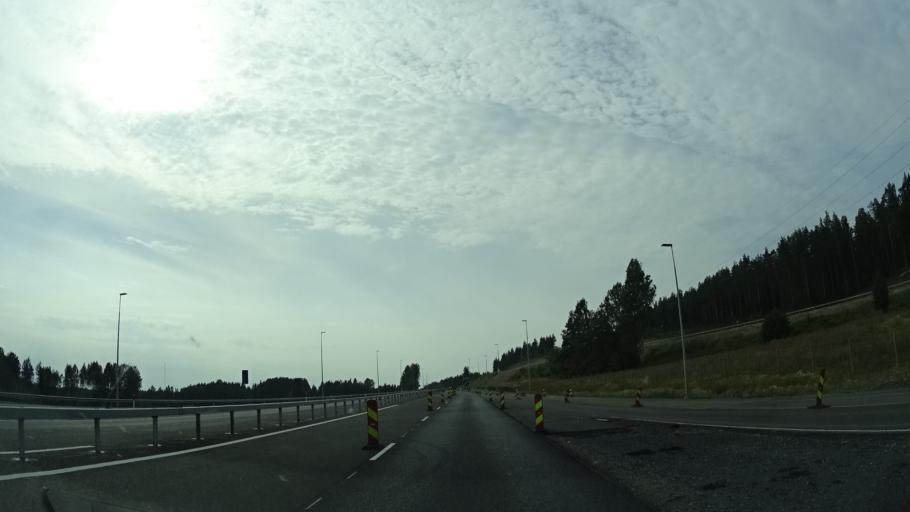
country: FI
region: South Karelia
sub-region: Lappeenranta
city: Luumaeki
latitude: 60.9382
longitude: 27.7006
